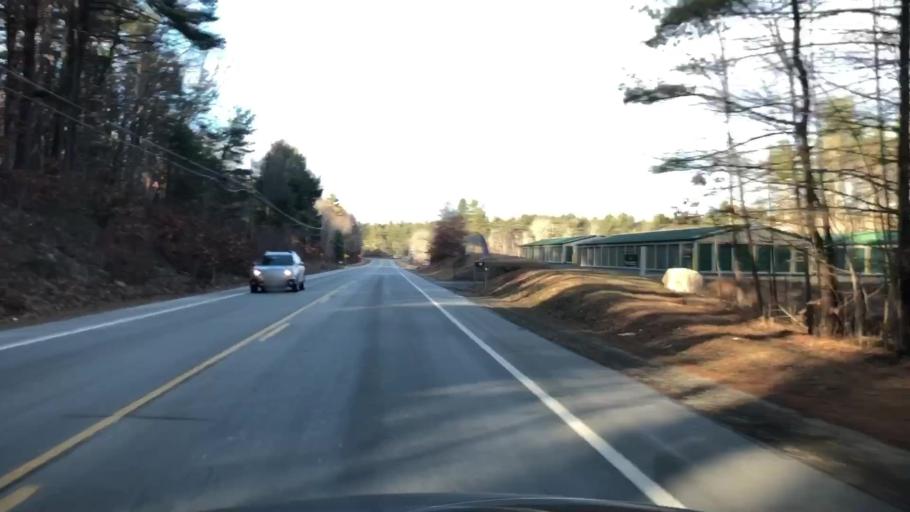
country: US
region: New Hampshire
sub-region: Hillsborough County
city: Brookline
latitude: 42.7189
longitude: -71.6625
